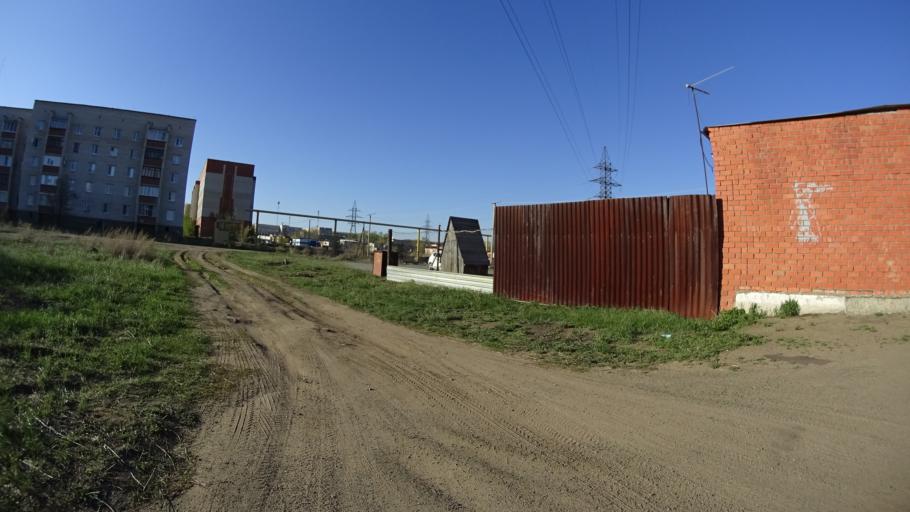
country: RU
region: Chelyabinsk
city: Troitsk
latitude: 54.0716
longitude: 61.5347
